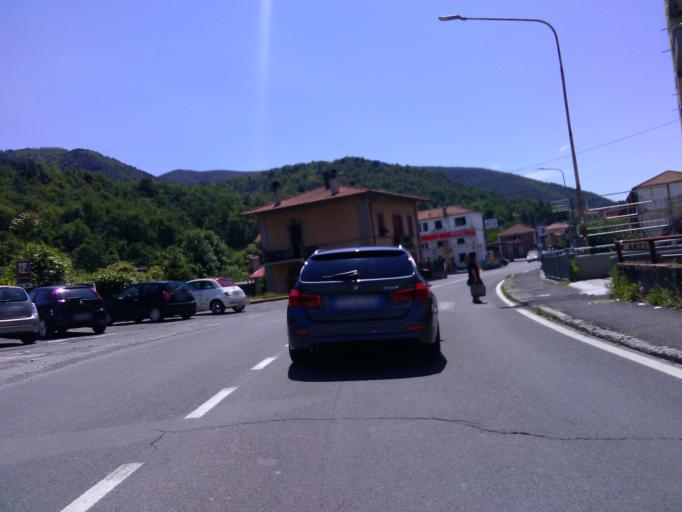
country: IT
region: Tuscany
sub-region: Provincia di Massa-Carrara
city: Aulla
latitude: 44.2056
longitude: 9.9699
